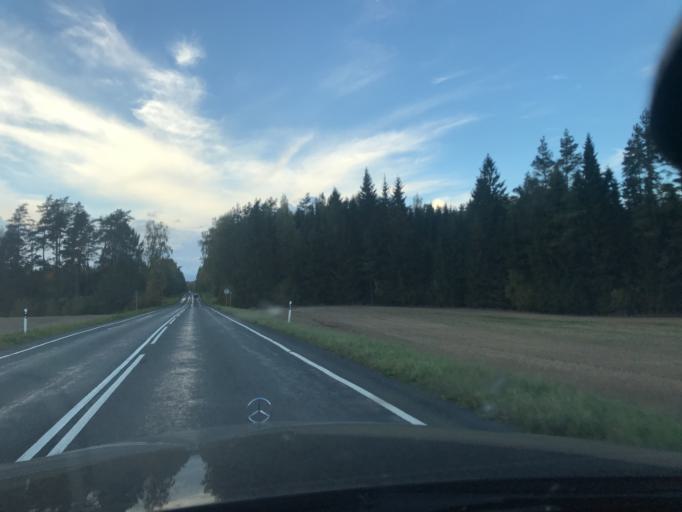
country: EE
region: Vorumaa
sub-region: Antsla vald
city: Vana-Antsla
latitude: 57.8728
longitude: 26.5925
